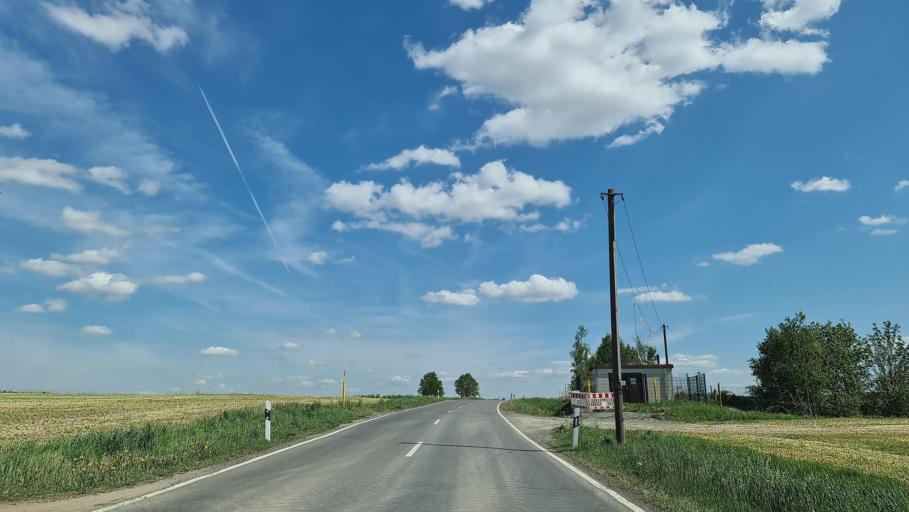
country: DE
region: Thuringia
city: Zeulenroda
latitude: 50.6308
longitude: 12.0223
